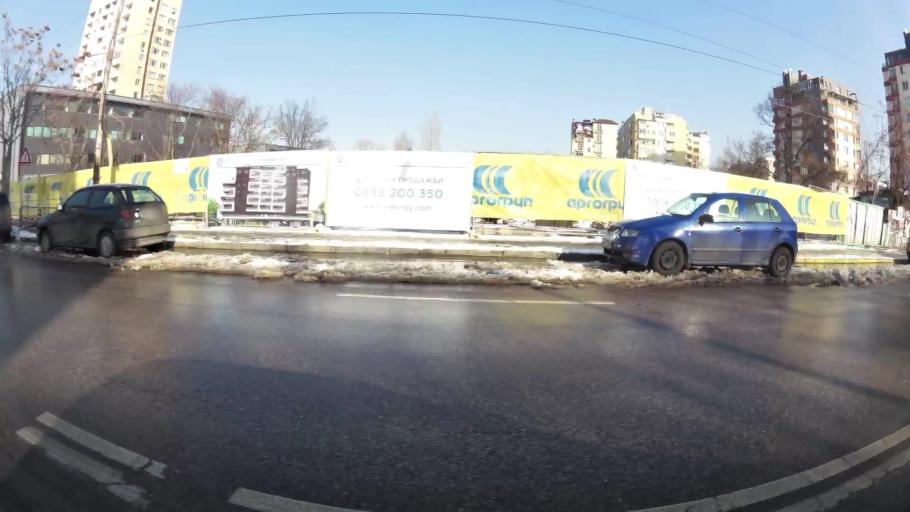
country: BG
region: Sofia-Capital
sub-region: Stolichna Obshtina
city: Sofia
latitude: 42.6634
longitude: 23.3446
